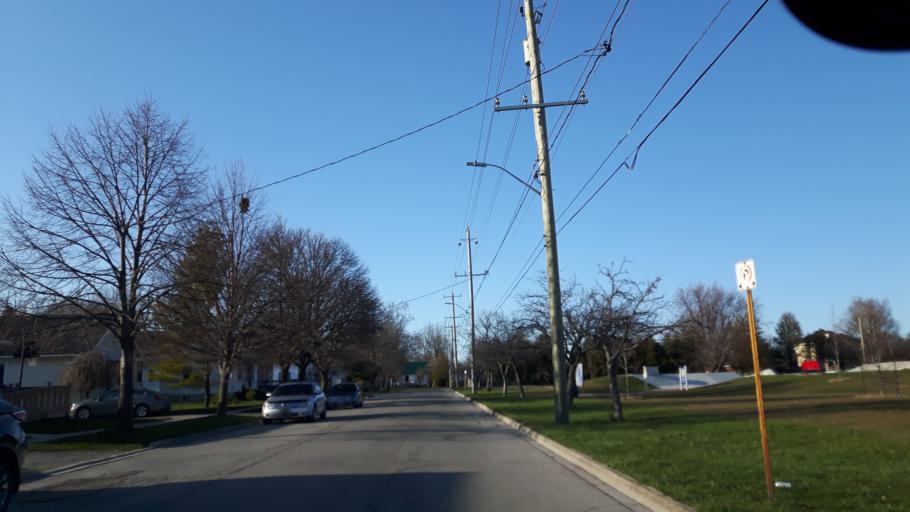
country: CA
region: Ontario
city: Goderich
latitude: 43.7375
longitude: -81.7164
